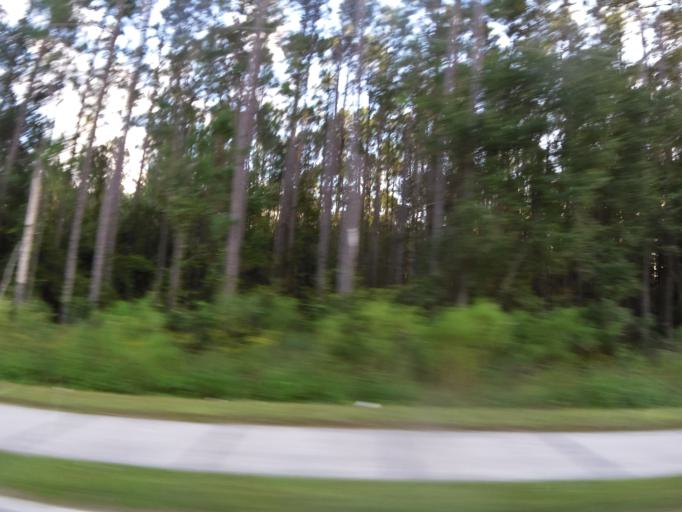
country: US
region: Florida
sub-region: Saint Johns County
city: Fruit Cove
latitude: 30.0598
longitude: -81.5215
